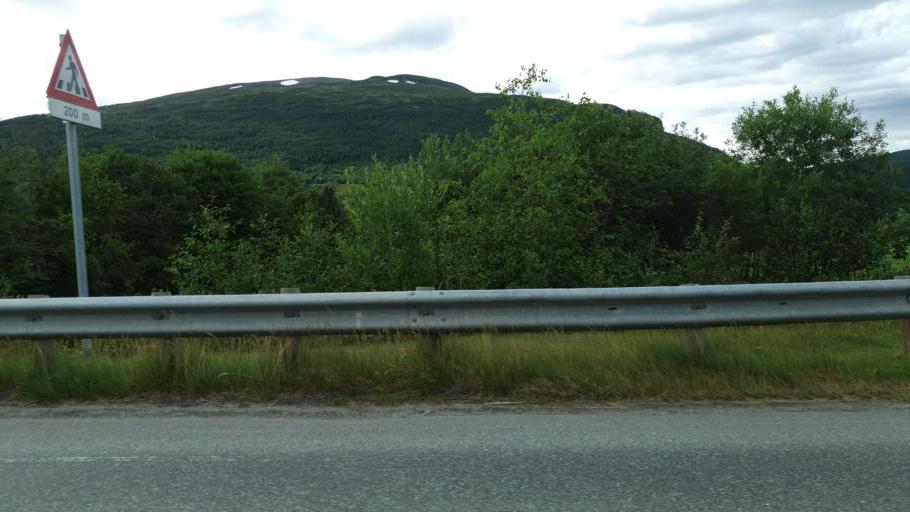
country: NO
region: Sor-Trondelag
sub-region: Oppdal
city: Oppdal
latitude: 62.5349
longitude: 9.6234
